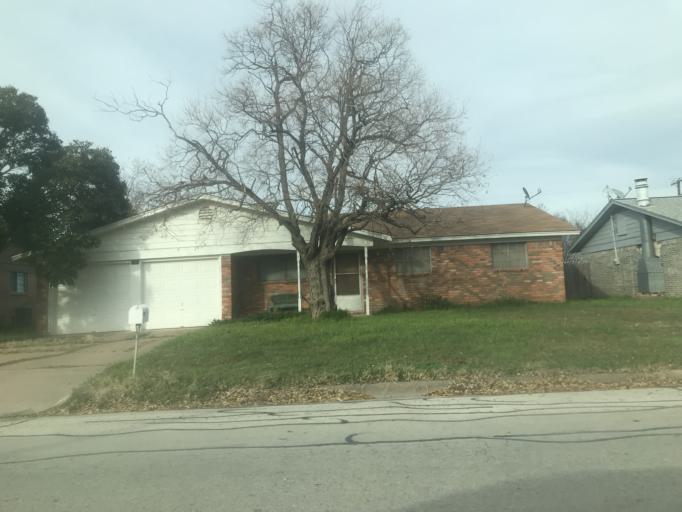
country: US
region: Texas
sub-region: Taylor County
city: Abilene
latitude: 32.3975
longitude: -99.7550
